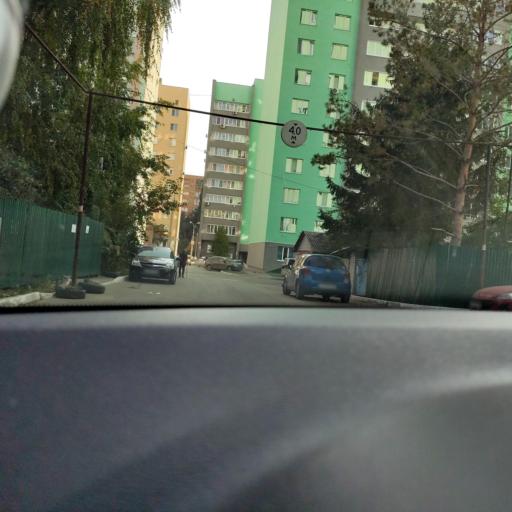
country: RU
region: Samara
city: Samara
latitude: 53.2352
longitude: 50.2574
